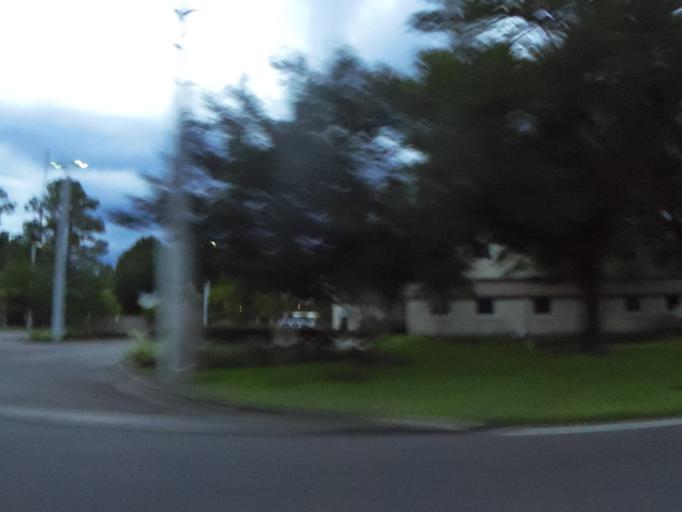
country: US
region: Florida
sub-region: Duval County
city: Jacksonville
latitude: 30.2641
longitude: -81.6120
